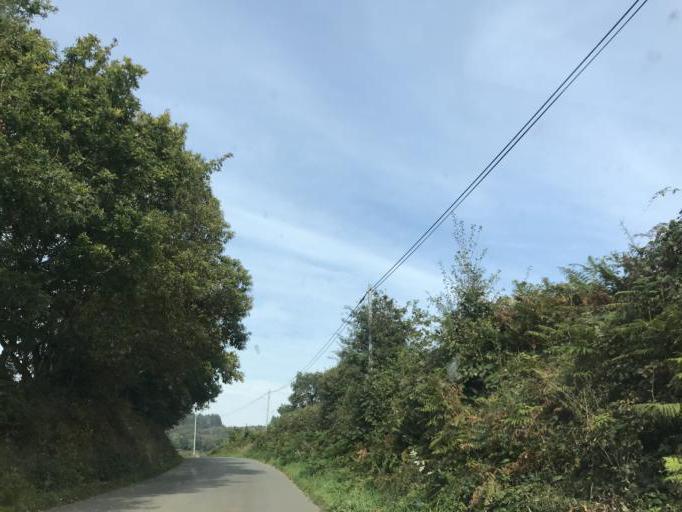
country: FR
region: Brittany
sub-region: Departement du Finistere
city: Brasparts
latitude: 48.3212
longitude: -3.9325
